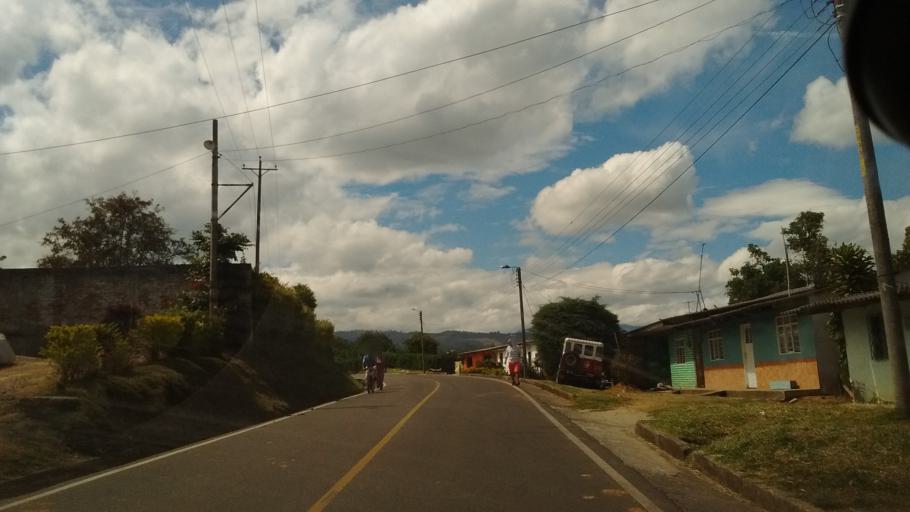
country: CO
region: Cauca
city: Cajibio
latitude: 2.6295
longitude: -76.5201
